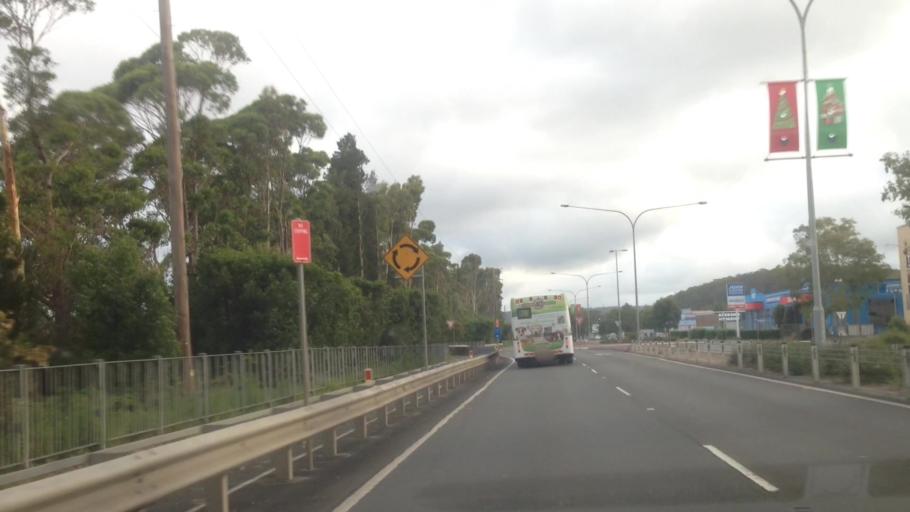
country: AU
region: New South Wales
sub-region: Wyong Shire
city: Chittaway Bay
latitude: -33.3025
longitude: 151.4210
